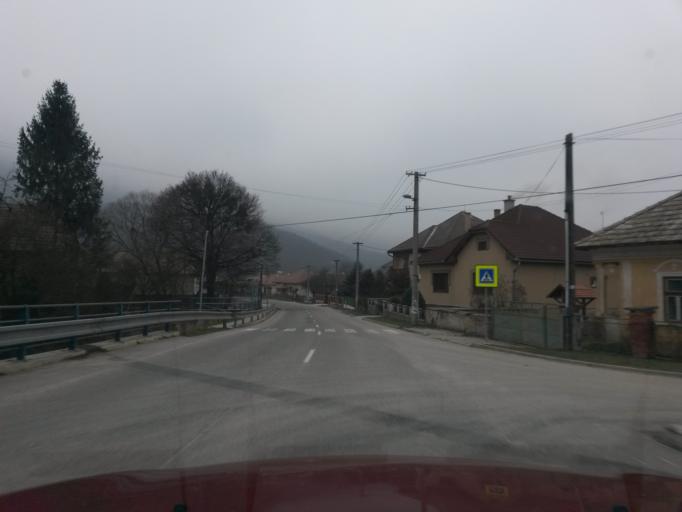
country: SK
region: Kosicky
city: Roznava
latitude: 48.6260
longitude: 20.5802
